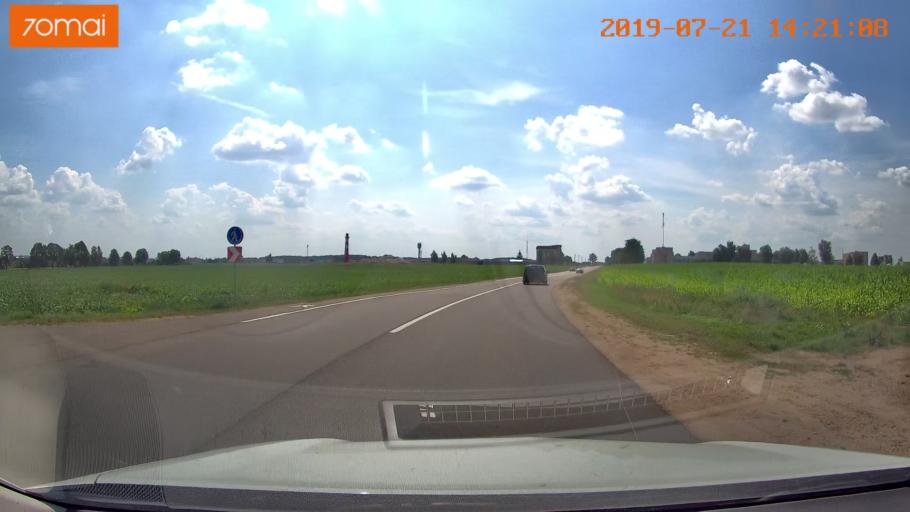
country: BY
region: Grodnenskaya
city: Karelichy
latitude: 53.5783
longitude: 26.1482
